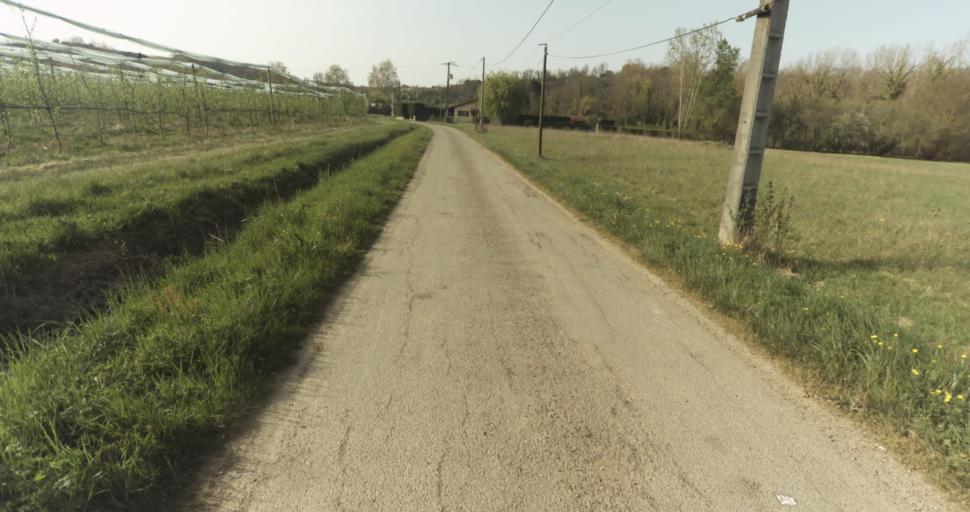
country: FR
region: Midi-Pyrenees
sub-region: Departement du Tarn-et-Garonne
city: Moissac
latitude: 44.1199
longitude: 1.1372
